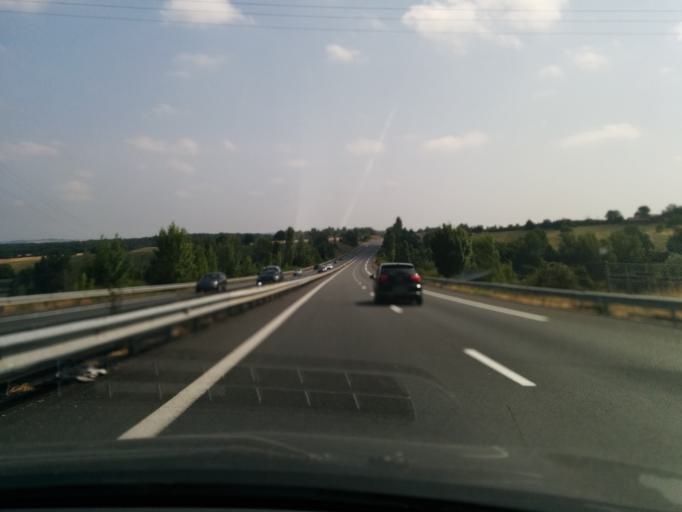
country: FR
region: Midi-Pyrenees
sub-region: Departement de la Haute-Garonne
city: Montastruc-la-Conseillere
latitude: 43.7353
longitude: 1.5819
